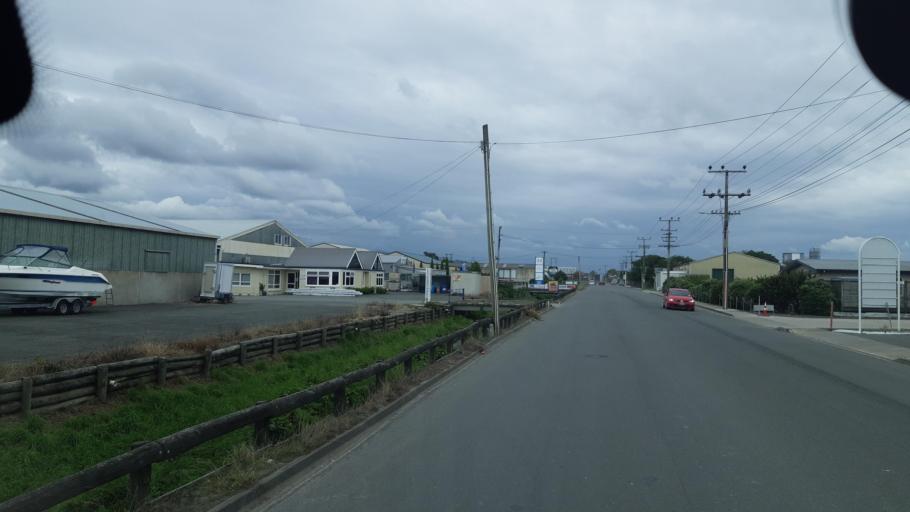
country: NZ
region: Tasman
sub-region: Tasman District
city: Richmond
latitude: -41.3326
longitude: 173.1882
